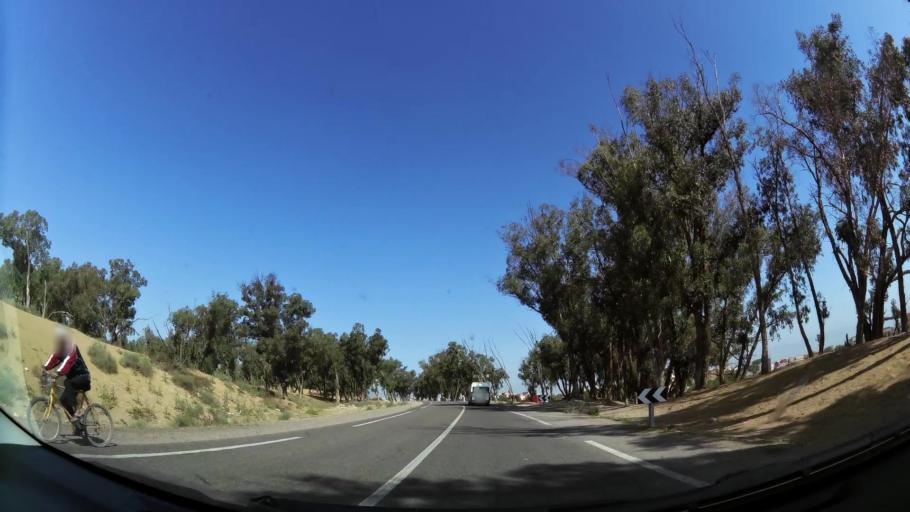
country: MA
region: Souss-Massa-Draa
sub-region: Inezgane-Ait Mellou
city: Inezgane
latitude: 30.3211
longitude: -9.5280
